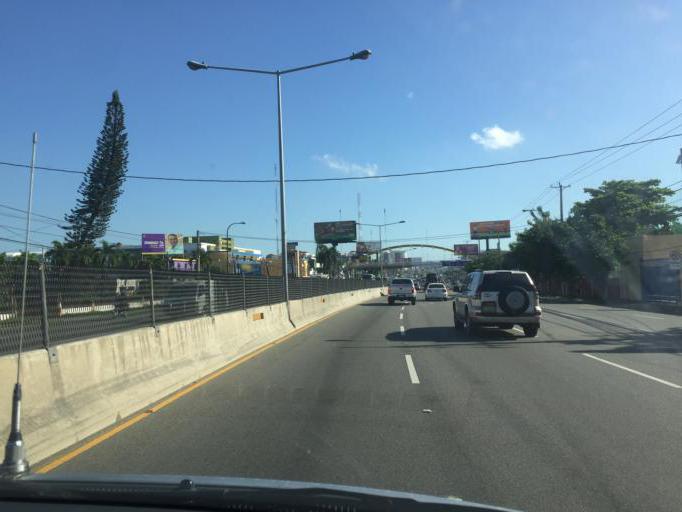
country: DO
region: Nacional
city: Bella Vista
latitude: 18.4561
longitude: -69.9521
